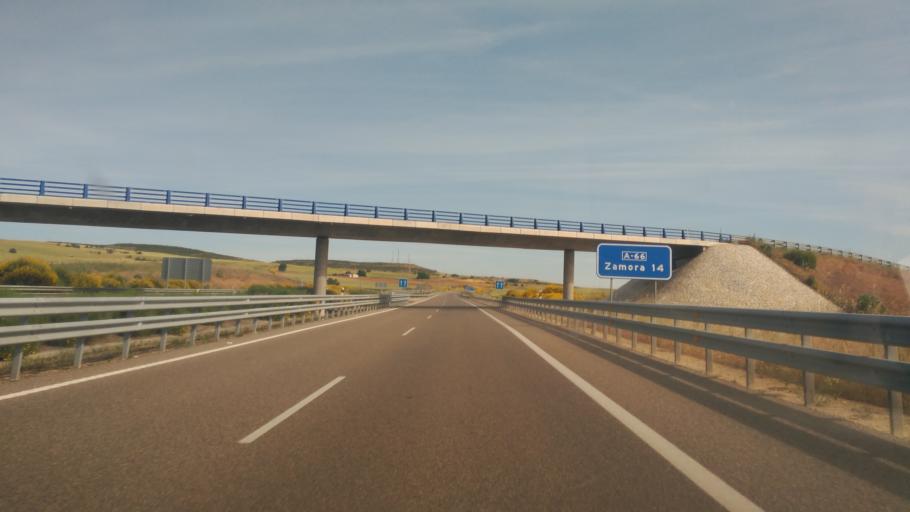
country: ES
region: Castille and Leon
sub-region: Provincia de Zamora
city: Corrales
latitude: 41.3656
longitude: -5.7154
